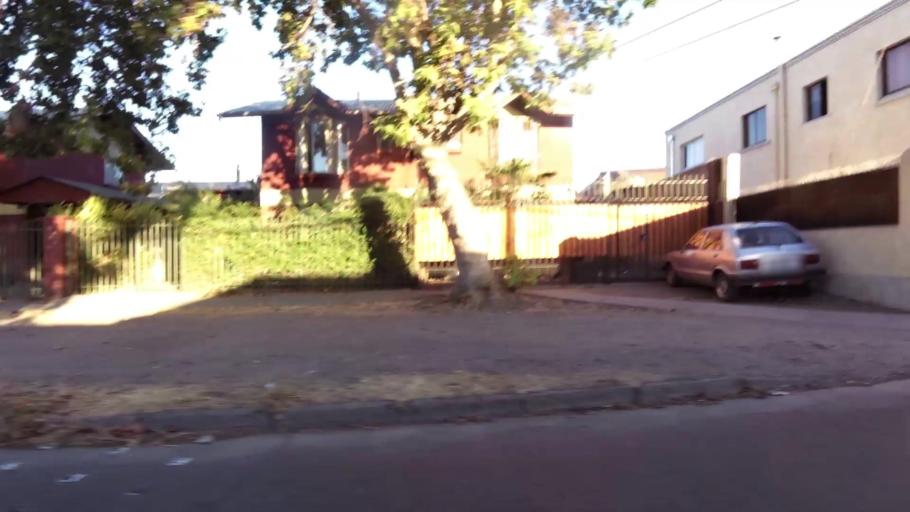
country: CL
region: O'Higgins
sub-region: Provincia de Cachapoal
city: Rancagua
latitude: -34.1709
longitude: -70.7557
